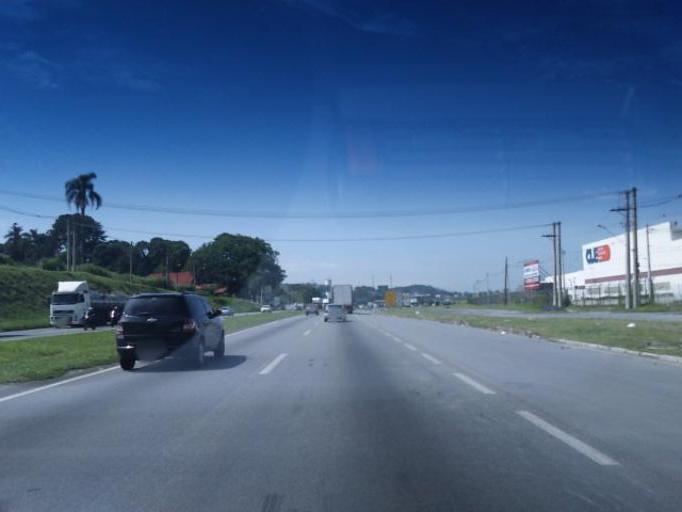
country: BR
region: Sao Paulo
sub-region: Embu
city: Embu
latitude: -23.6735
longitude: -46.8566
